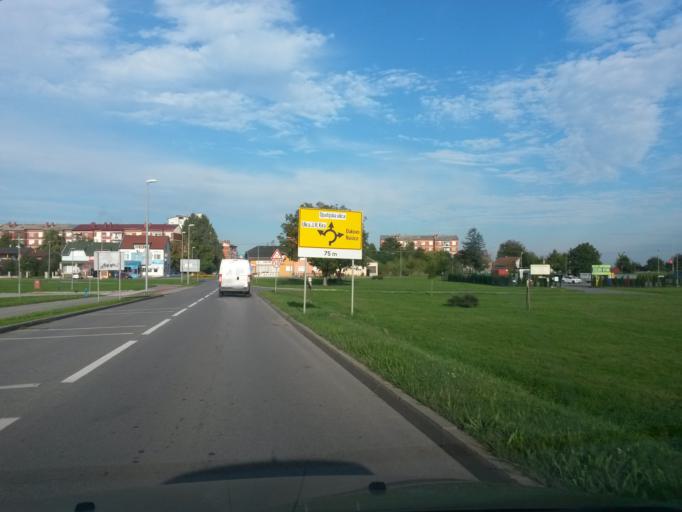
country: HR
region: Osjecko-Baranjska
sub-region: Grad Osijek
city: Osijek
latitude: 45.5423
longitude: 18.7096
